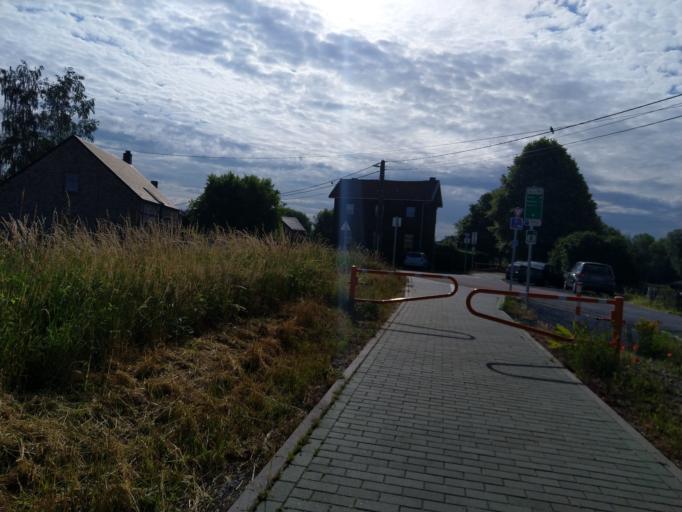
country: BE
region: Wallonia
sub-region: Province du Hainaut
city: Erquelinnes
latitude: 50.3144
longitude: 4.1149
